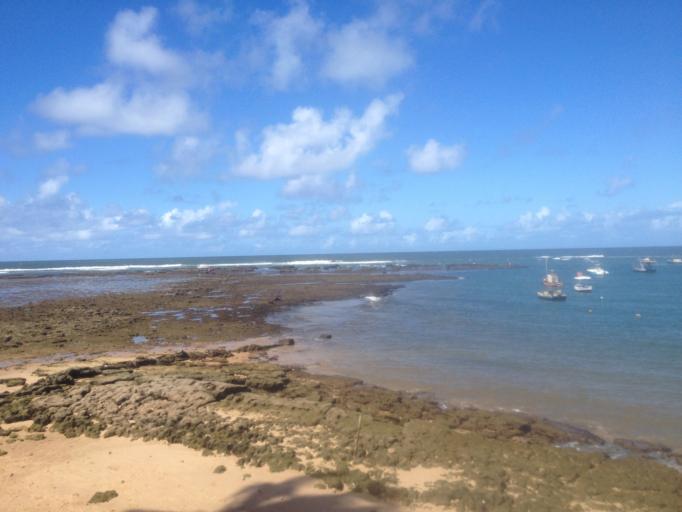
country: BR
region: Bahia
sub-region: Mata De Sao Joao
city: Mata de Sao Joao
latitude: -12.5779
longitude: -38.0024
